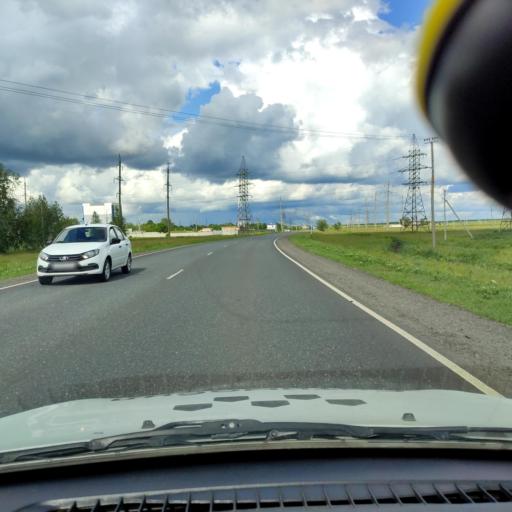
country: RU
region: Samara
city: Povolzhskiy
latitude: 53.6539
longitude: 49.6940
